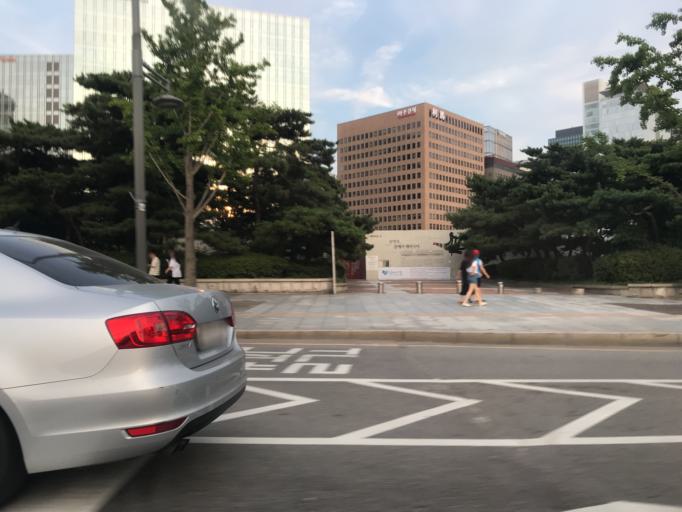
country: KR
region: Seoul
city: Seoul
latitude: 37.5753
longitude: 126.9776
